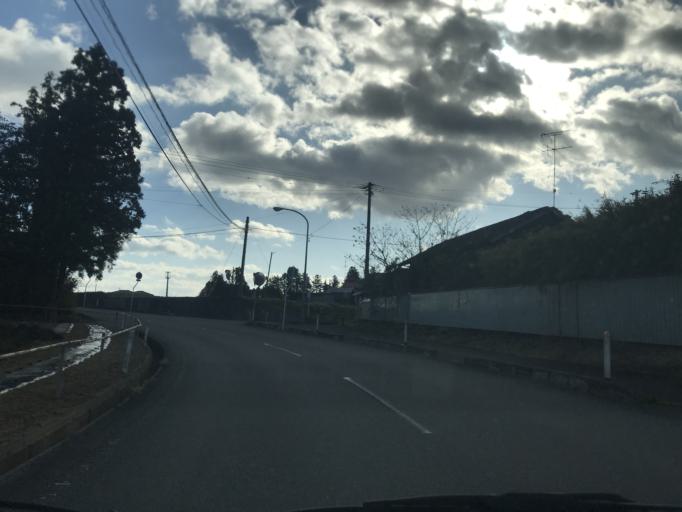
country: JP
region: Iwate
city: Ichinoseki
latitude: 38.7593
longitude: 141.0594
